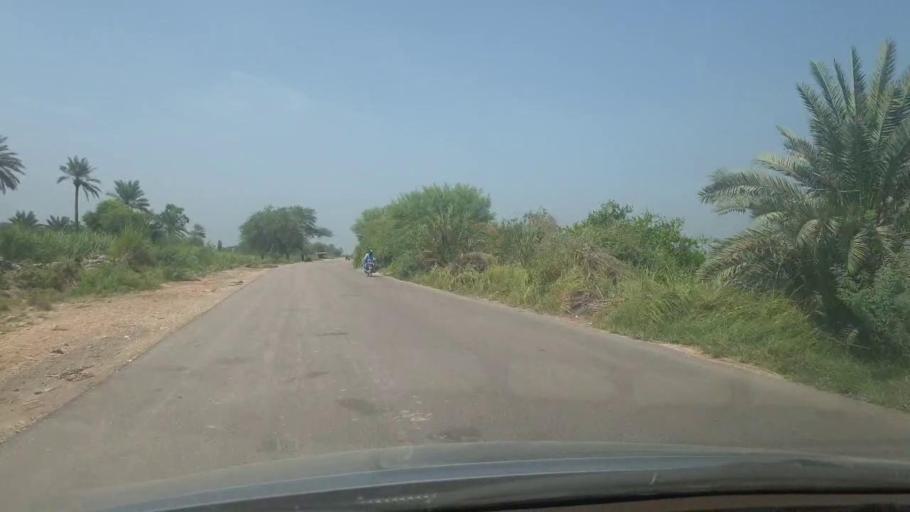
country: PK
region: Sindh
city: Ranipur
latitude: 27.2483
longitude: 68.5807
